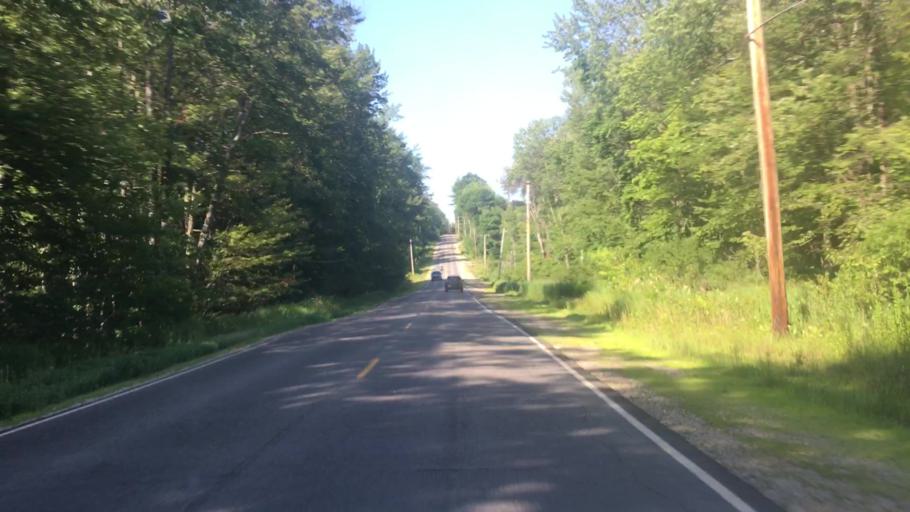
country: US
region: Maine
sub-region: York County
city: Buxton
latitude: 43.7057
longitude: -70.5781
